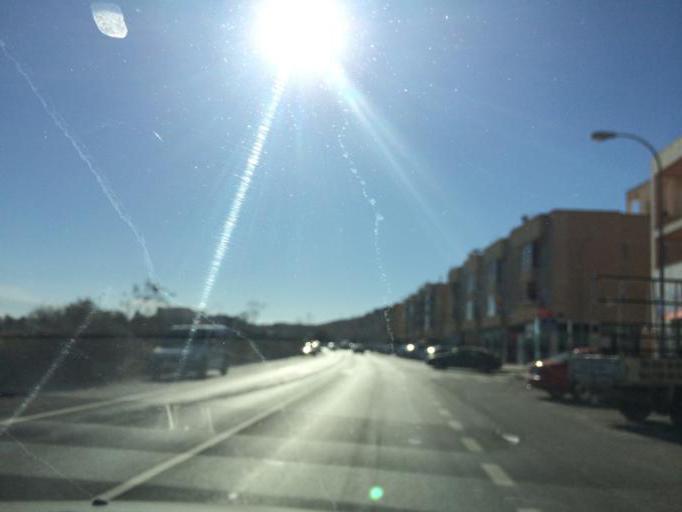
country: ES
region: Andalusia
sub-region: Provincia de Almeria
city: Huercal de Almeria
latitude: 36.8762
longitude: -2.4397
